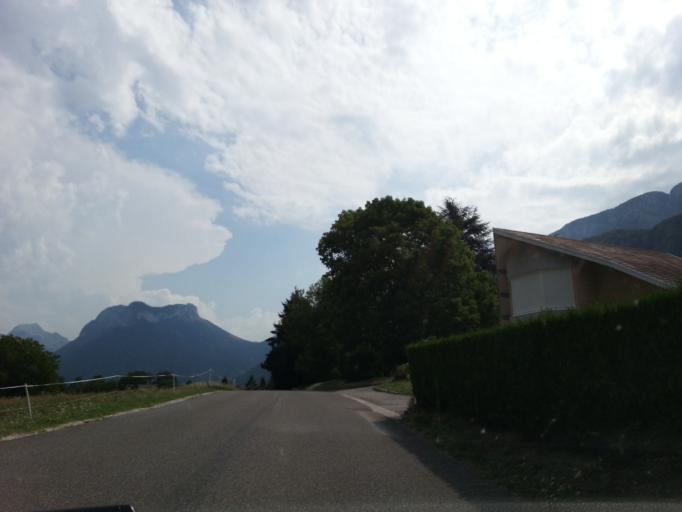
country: FR
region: Rhone-Alpes
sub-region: Departement de la Haute-Savoie
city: Talloires
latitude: 45.8081
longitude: 6.2093
